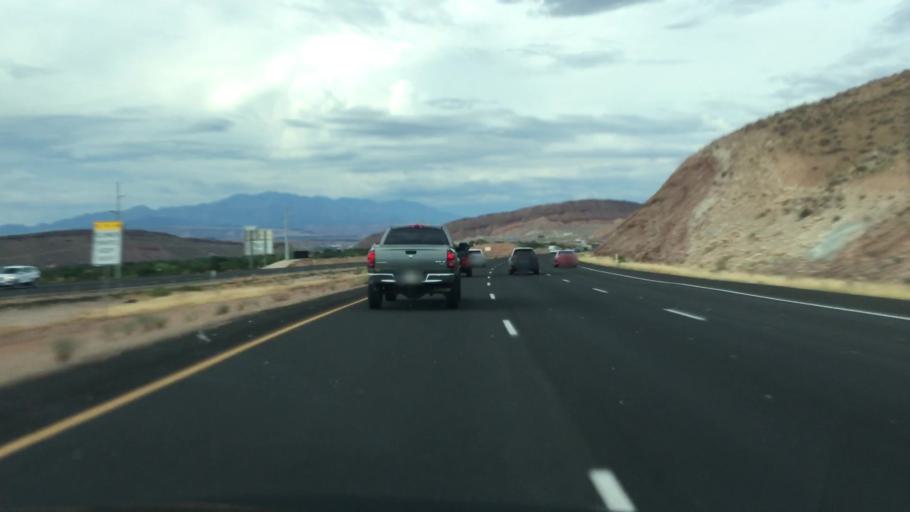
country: US
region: Utah
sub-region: Washington County
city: Saint George
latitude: 37.0369
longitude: -113.5987
